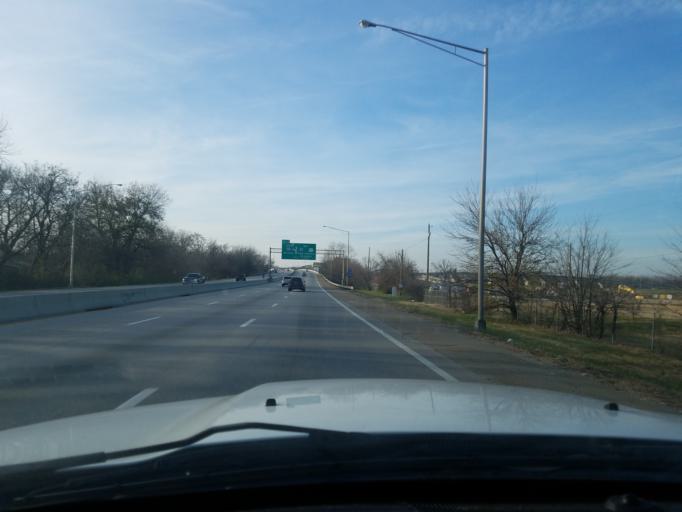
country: US
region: Kentucky
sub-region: Jefferson County
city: Louisville
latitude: 38.2737
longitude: -85.7866
